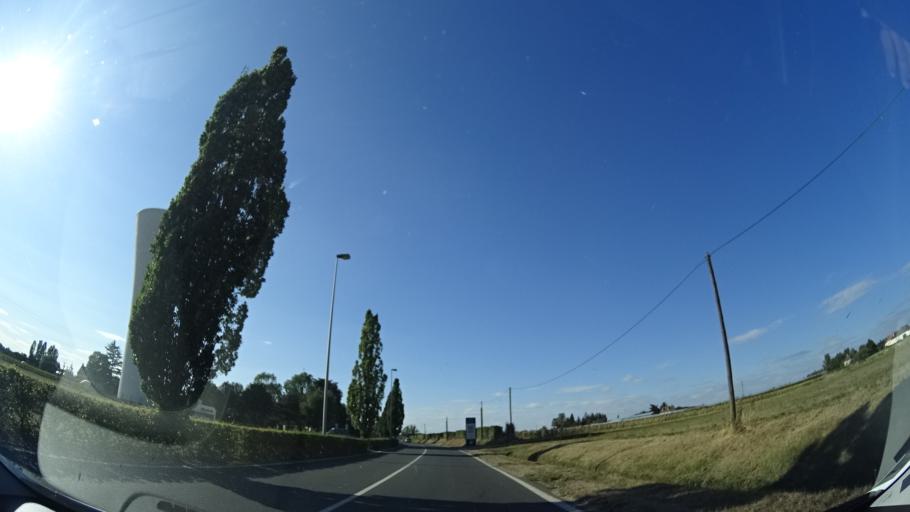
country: FR
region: Centre
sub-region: Departement du Loiret
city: Saint-Jean-de-Braye
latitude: 47.9182
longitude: 1.9612
